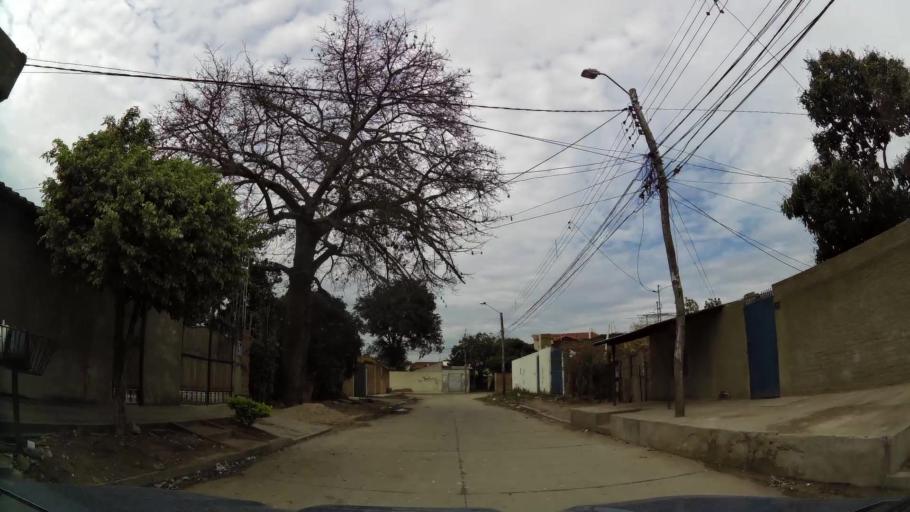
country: BO
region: Santa Cruz
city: Santa Cruz de la Sierra
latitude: -17.7455
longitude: -63.1935
